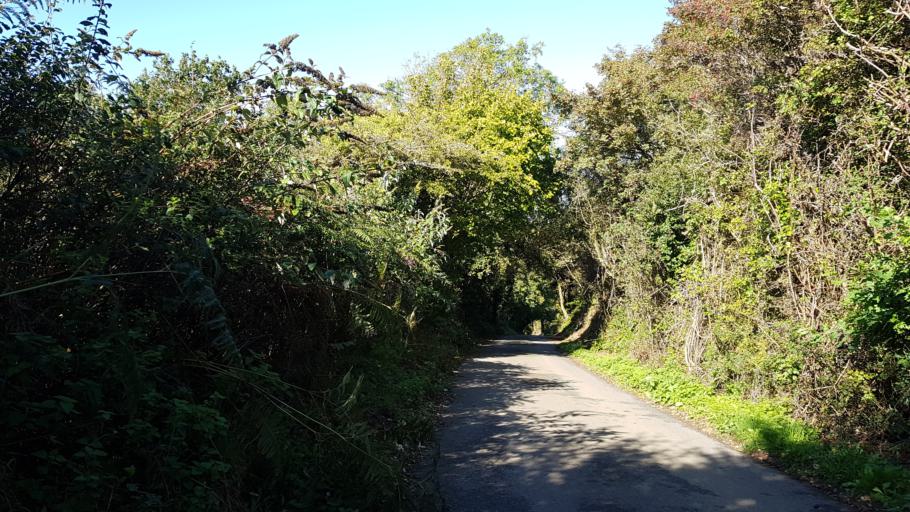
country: GB
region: England
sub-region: Isle of Wight
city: Newport
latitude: 50.6865
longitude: -1.2831
